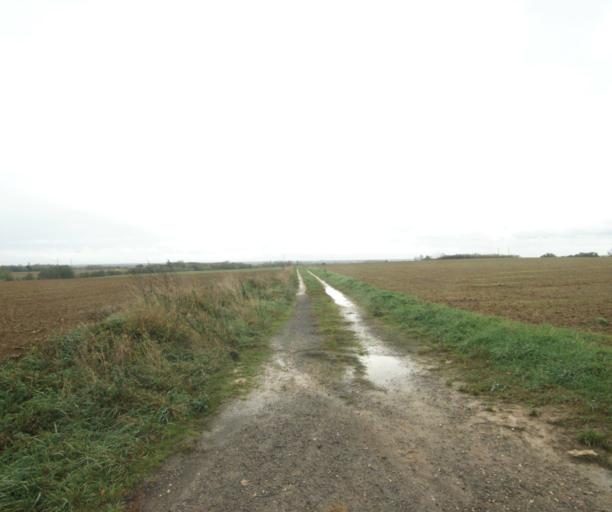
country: FR
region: Rhone-Alpes
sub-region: Departement de l'Ain
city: Pont-de-Vaux
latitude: 46.4887
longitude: 4.8818
